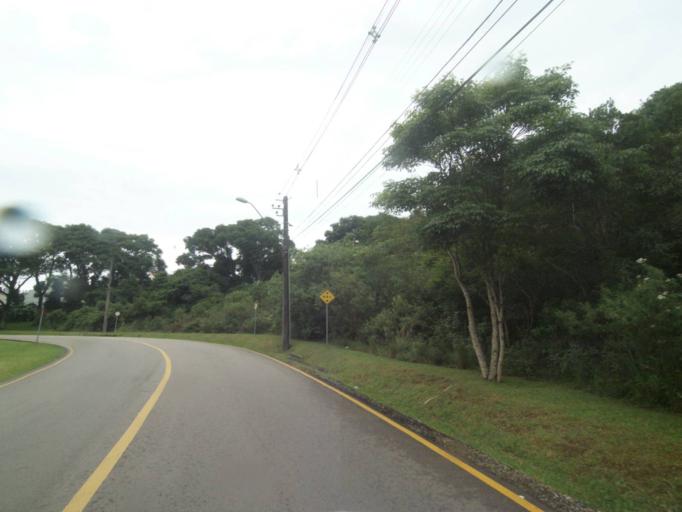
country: BR
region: Parana
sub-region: Curitiba
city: Curitiba
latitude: -25.4276
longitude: -49.3144
